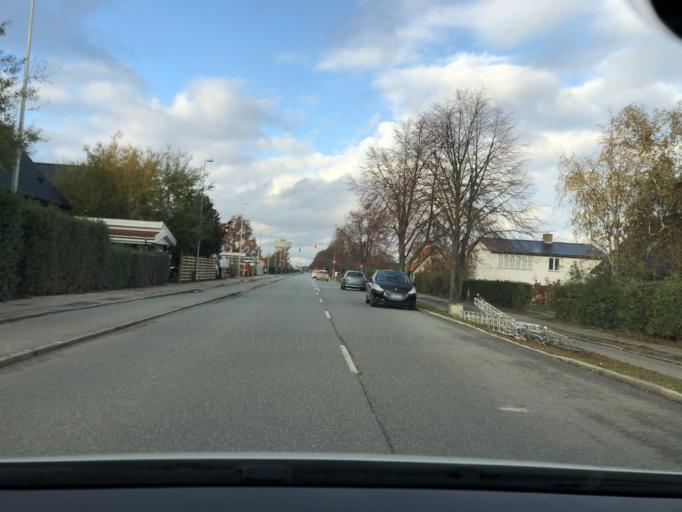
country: DK
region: Capital Region
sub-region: Tarnby Kommune
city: Tarnby
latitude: 55.6163
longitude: 12.5927
